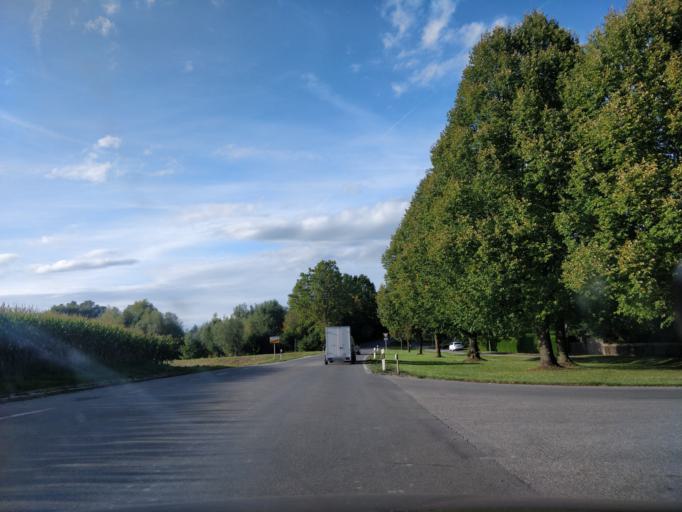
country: DE
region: Bavaria
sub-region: Swabia
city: Friedberg
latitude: 48.3437
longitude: 10.9951
